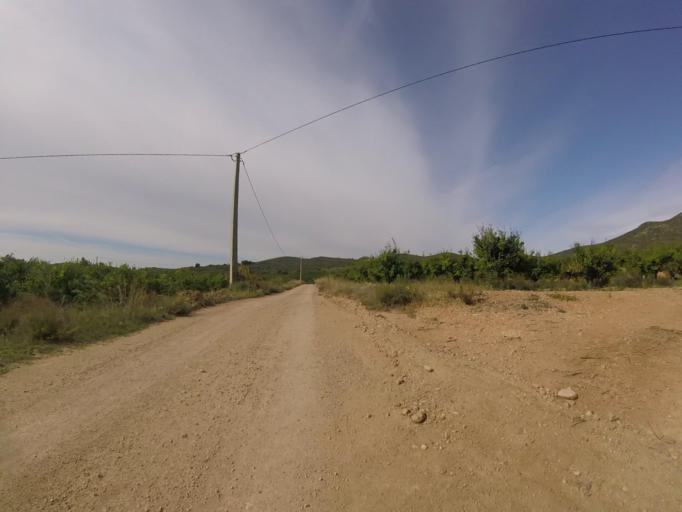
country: ES
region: Valencia
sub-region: Provincia de Castello
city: Torreblanca
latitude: 40.1962
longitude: 0.1613
